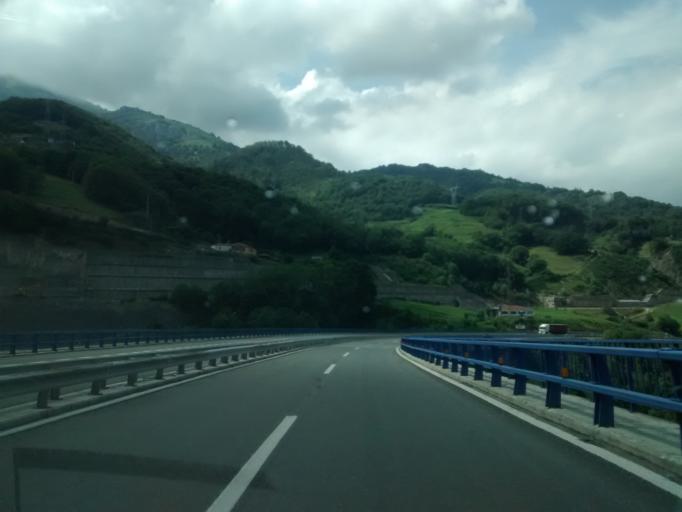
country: ES
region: Asturias
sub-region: Province of Asturias
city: Pola de Lena
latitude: 43.1038
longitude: -5.8200
